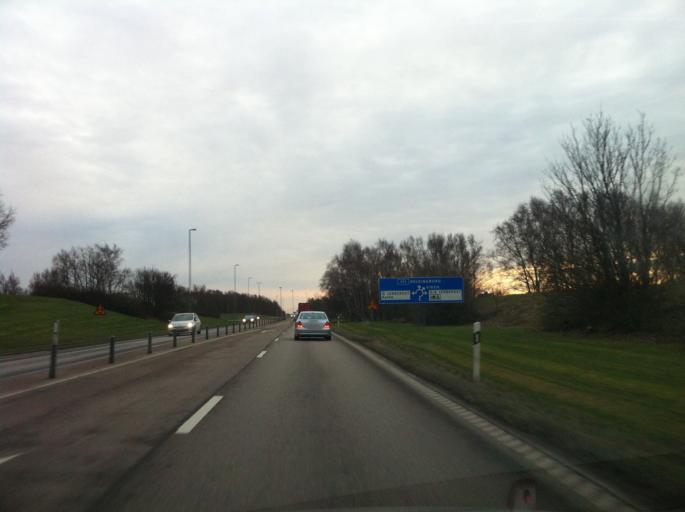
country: SE
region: Skane
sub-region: Hoganas Kommun
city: Hoganas
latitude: 56.1749
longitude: 12.5633
